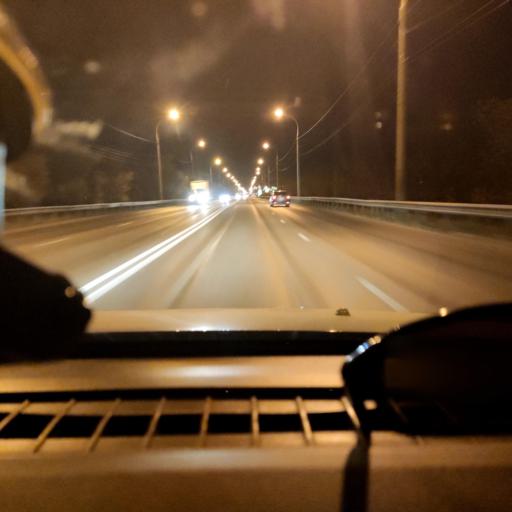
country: RU
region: Samara
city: Samara
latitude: 53.1491
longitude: 50.1852
